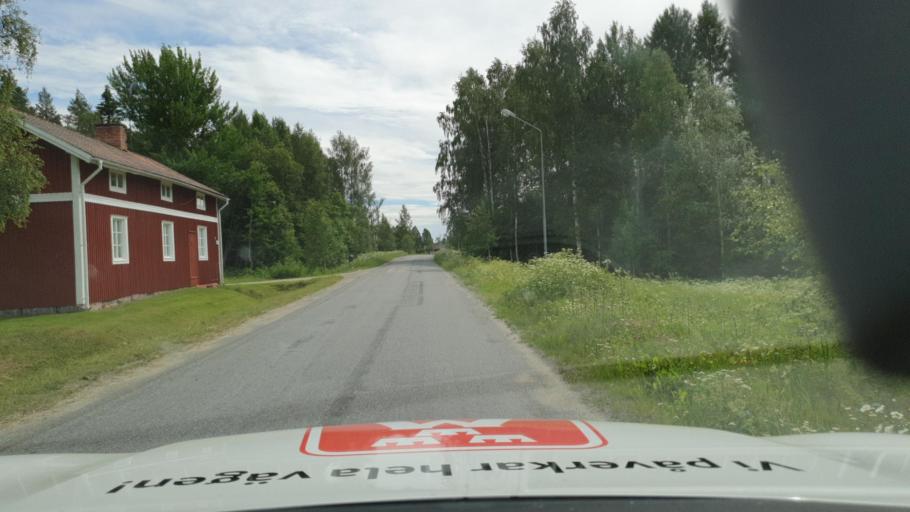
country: SE
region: Vaesterbotten
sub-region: Skelleftea Kommun
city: Burtraesk
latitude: 64.4923
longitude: 20.5046
